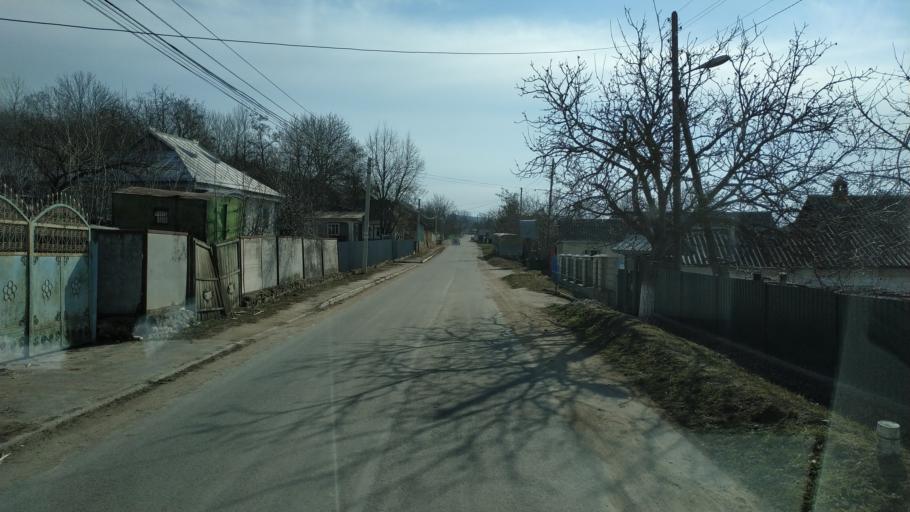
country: MD
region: Nisporeni
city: Nisporeni
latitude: 47.1766
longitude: 28.1247
